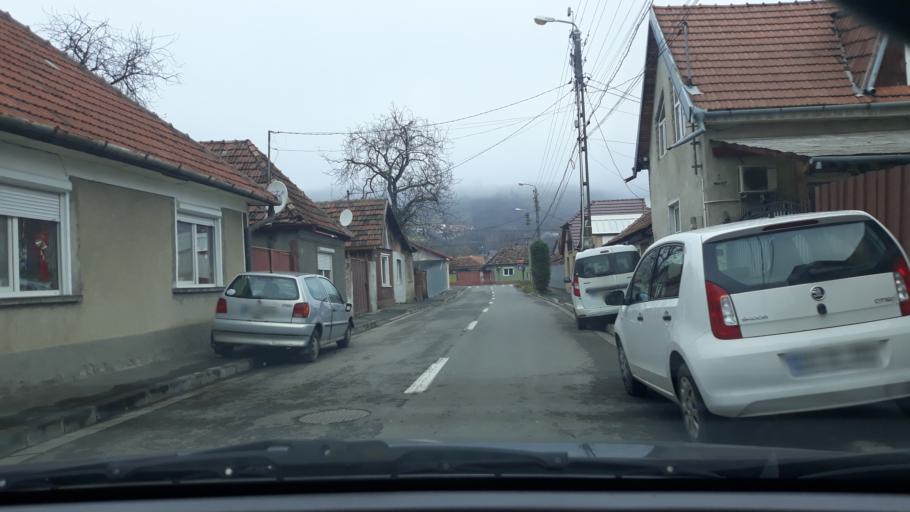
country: RO
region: Bihor
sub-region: Comuna Sanmartin
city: Sanmartin
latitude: 47.0486
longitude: 21.9727
